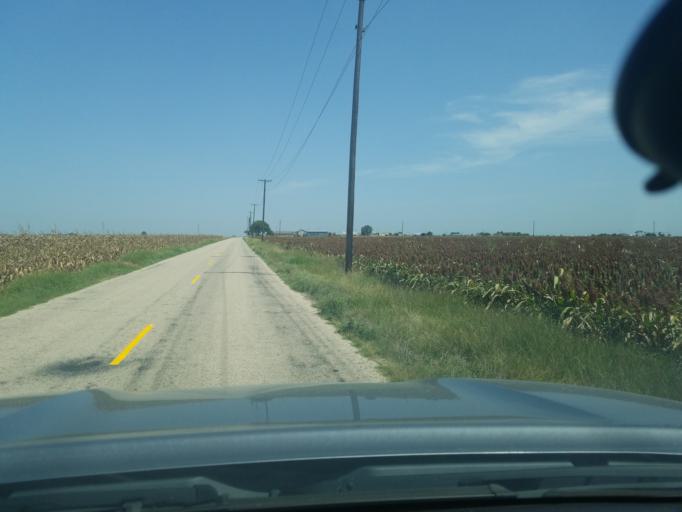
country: US
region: Texas
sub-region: Guadalupe County
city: Lake Dunlap
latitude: 29.6839
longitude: -98.0321
